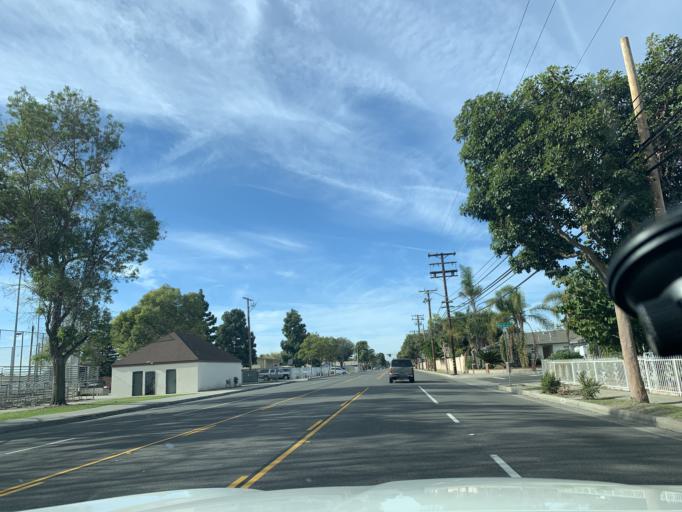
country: US
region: California
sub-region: Orange County
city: Garden Grove
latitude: 33.7525
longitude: -117.9302
